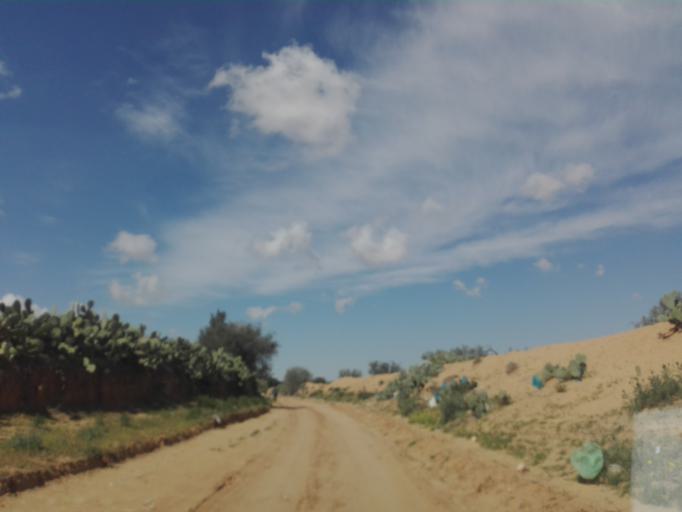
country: TN
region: Safaqis
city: Sfax
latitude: 34.7347
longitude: 10.5157
